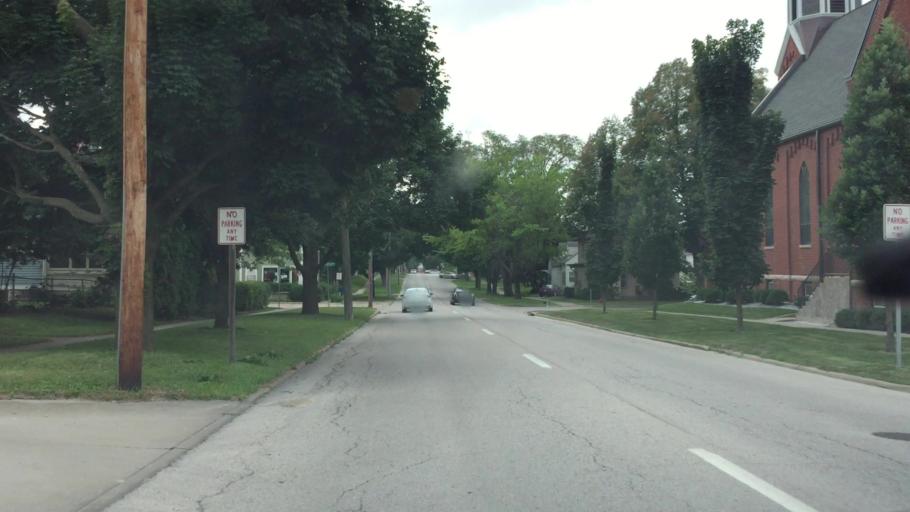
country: US
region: Iowa
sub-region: Johnson County
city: Iowa City
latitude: 41.6663
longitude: -91.5257
